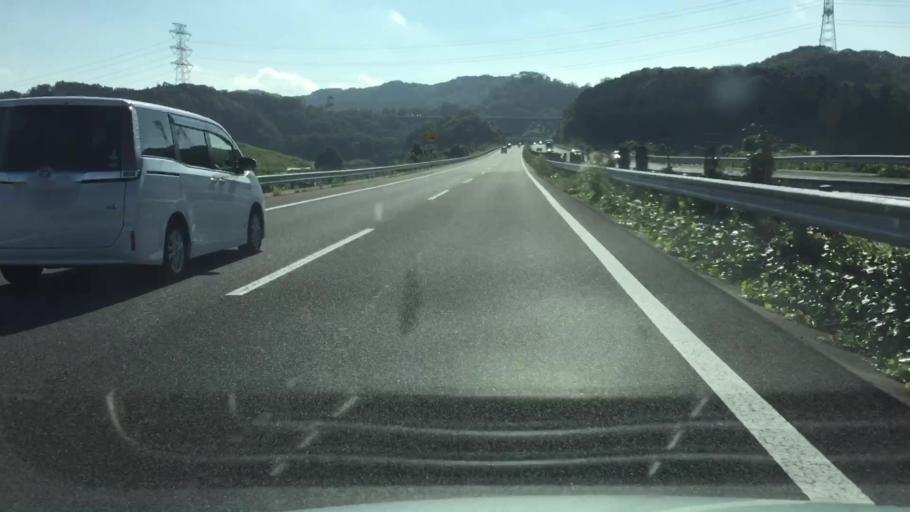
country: JP
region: Tochigi
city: Mooka
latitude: 36.3848
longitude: 140.0263
